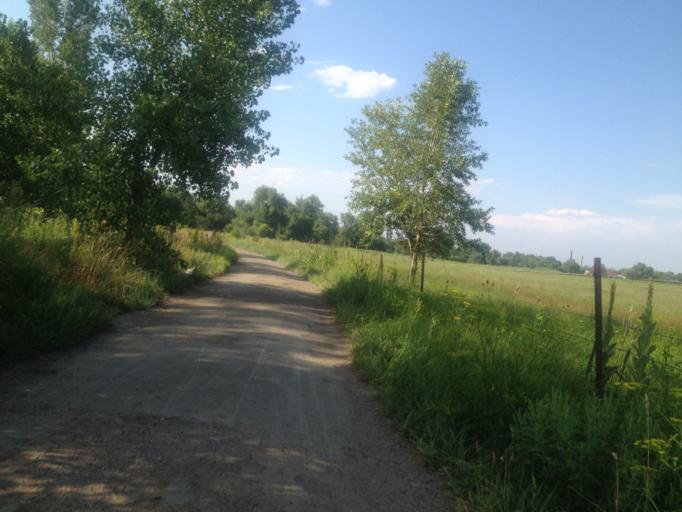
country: US
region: Colorado
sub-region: Boulder County
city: Boulder
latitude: 39.9913
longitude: -105.2166
